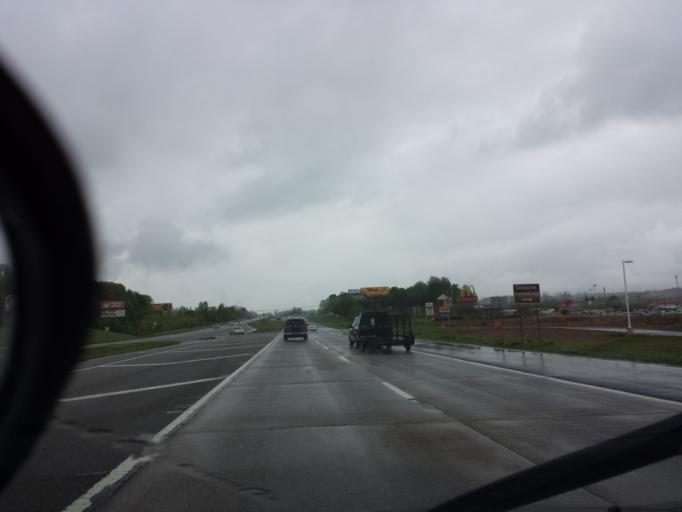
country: US
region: Georgia
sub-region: Pickens County
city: Jasper
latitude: 34.4612
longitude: -84.4562
